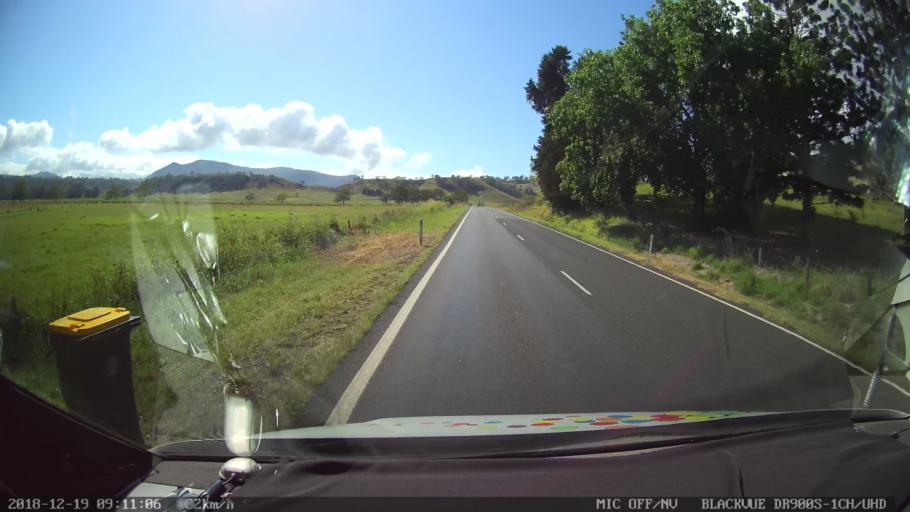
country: AU
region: New South Wales
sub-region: Kyogle
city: Kyogle
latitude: -28.4904
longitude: 152.9352
